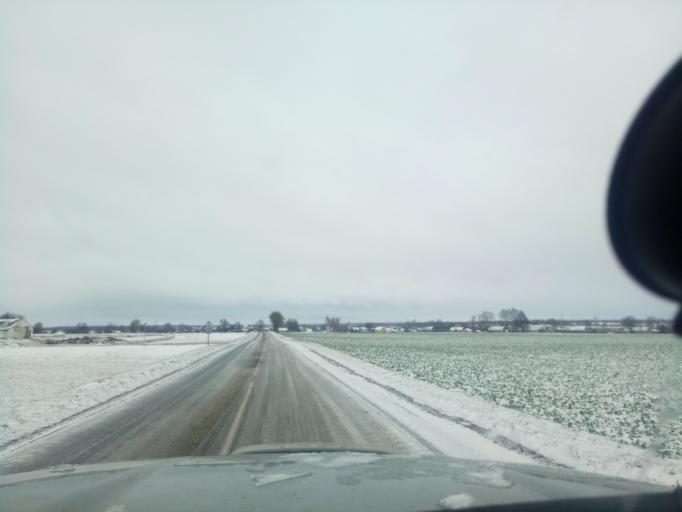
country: BY
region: Minsk
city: Klyetsk
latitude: 53.0407
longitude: 26.7475
